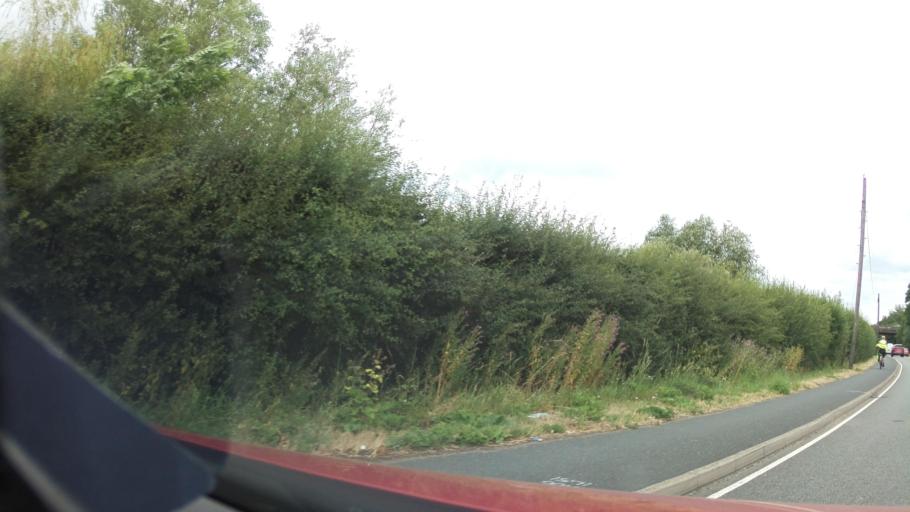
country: GB
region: England
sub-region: Leicestershire
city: Castle Donington
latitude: 52.8687
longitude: -1.3103
